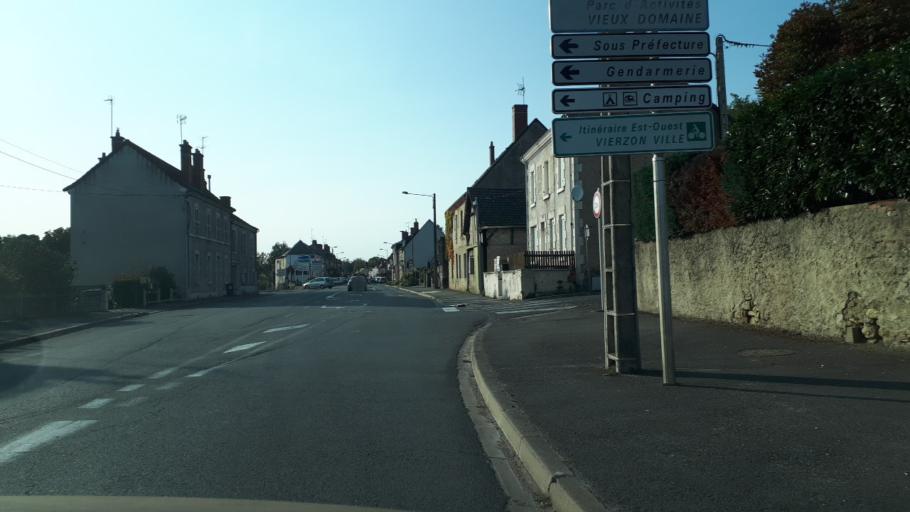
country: FR
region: Centre
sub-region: Departement du Cher
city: Vierzon
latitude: 47.2160
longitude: 2.1046
